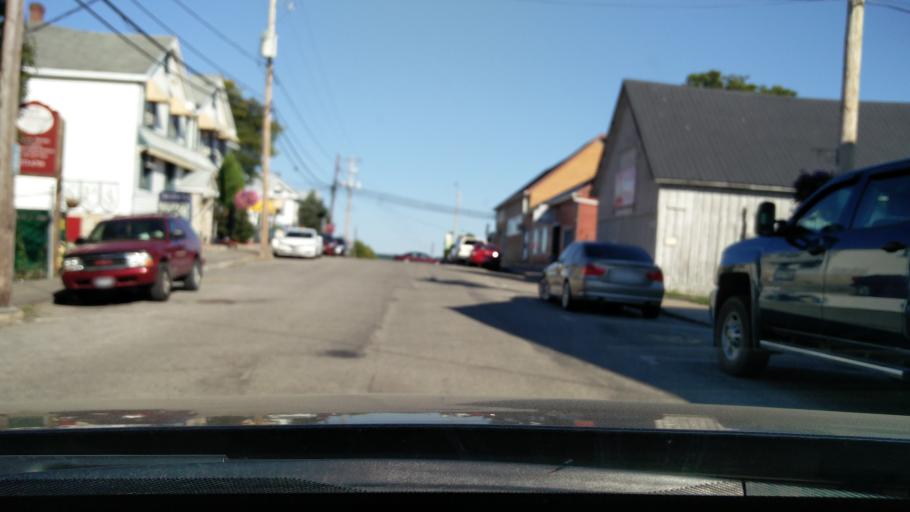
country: CA
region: Ontario
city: Perth
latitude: 44.6796
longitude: -76.3959
